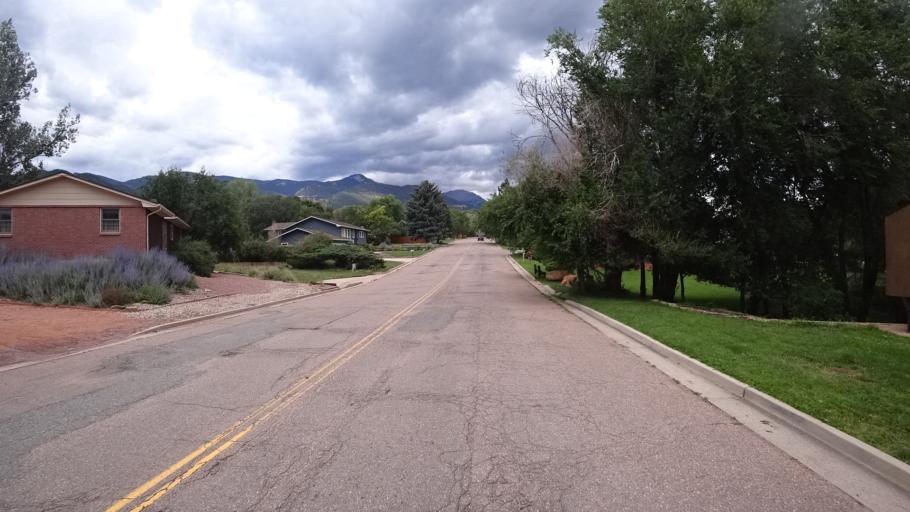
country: US
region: Colorado
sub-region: El Paso County
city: Manitou Springs
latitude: 38.8500
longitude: -104.8909
